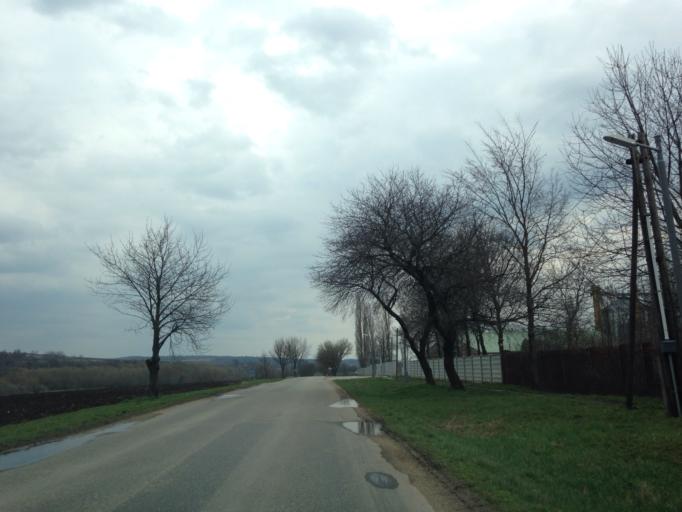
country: SK
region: Nitriansky
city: Svodin
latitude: 47.9820
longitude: 18.4018
